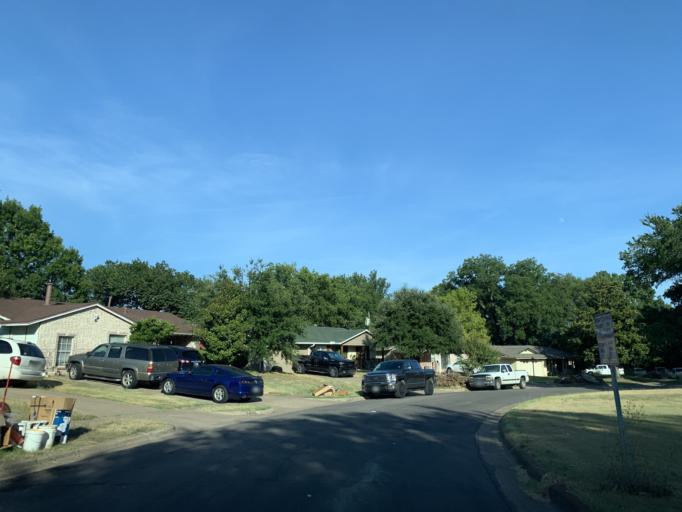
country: US
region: Texas
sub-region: Dallas County
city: Cockrell Hill
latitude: 32.7102
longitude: -96.8998
